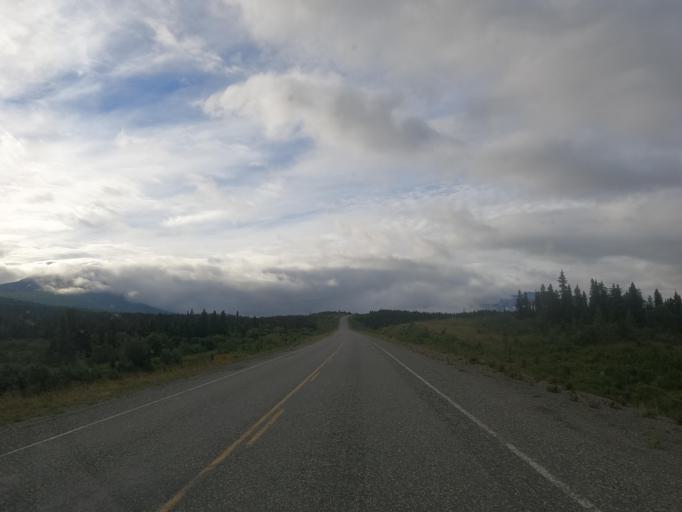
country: CA
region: Yukon
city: Haines Junction
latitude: 59.9526
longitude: -136.8075
